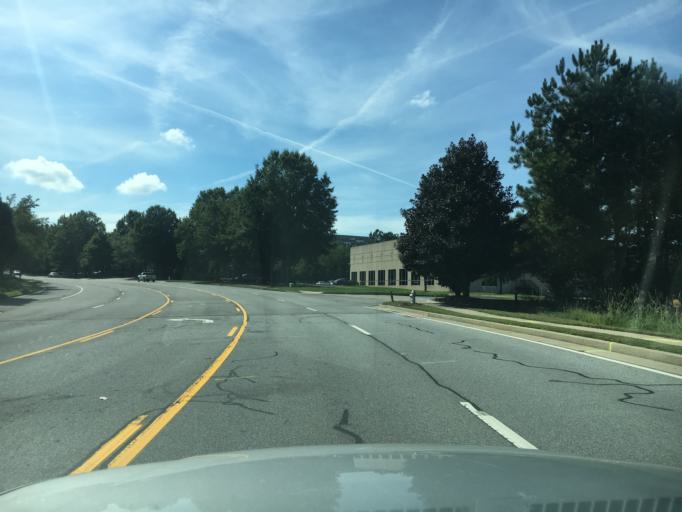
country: US
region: Georgia
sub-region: Gwinnett County
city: Duluth
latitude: 33.9683
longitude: -84.1184
